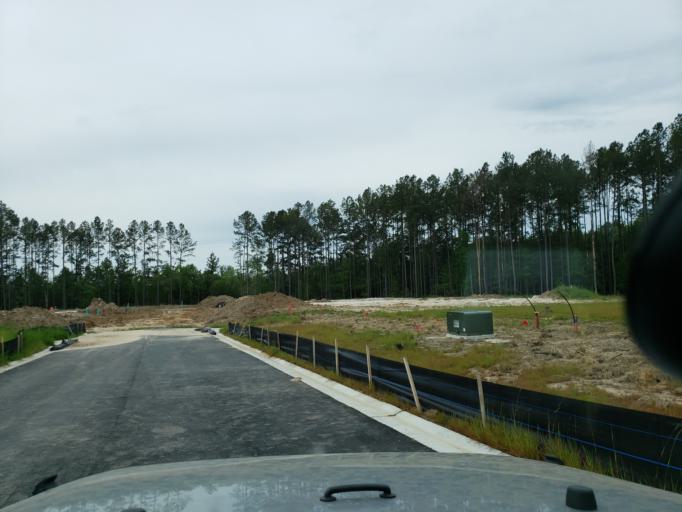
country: US
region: Georgia
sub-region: Chatham County
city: Port Wentworth
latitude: 32.2133
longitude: -81.1854
